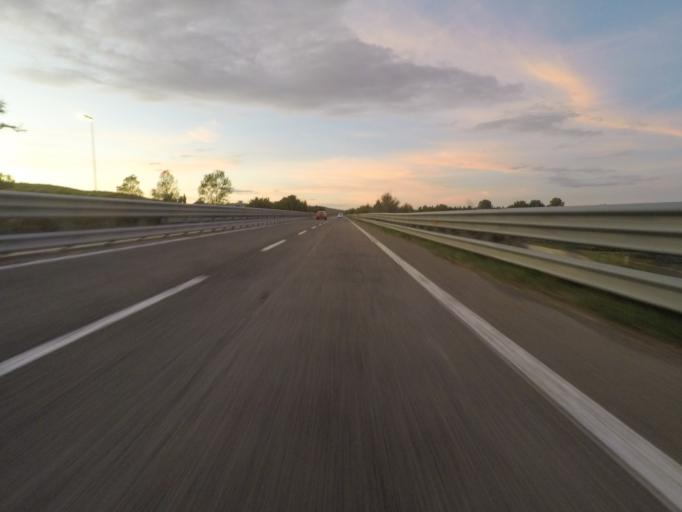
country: IT
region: Tuscany
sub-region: Provincia di Siena
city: Sinalunga
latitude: 43.2409
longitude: 11.7240
